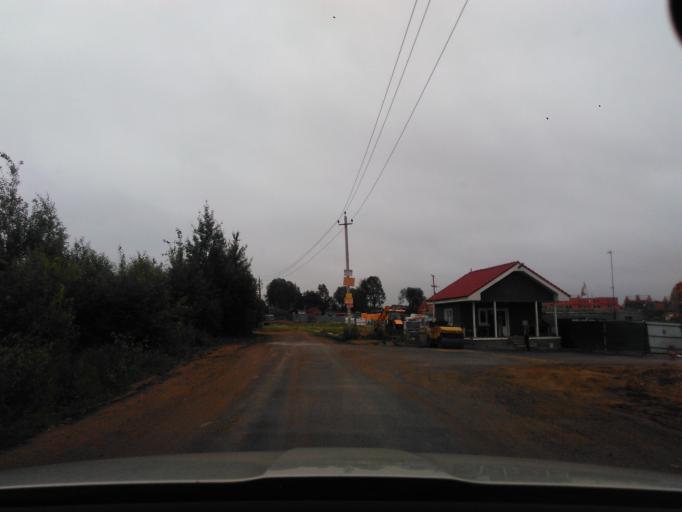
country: RU
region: Moskovskaya
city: Firsanovka
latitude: 55.9455
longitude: 37.2289
